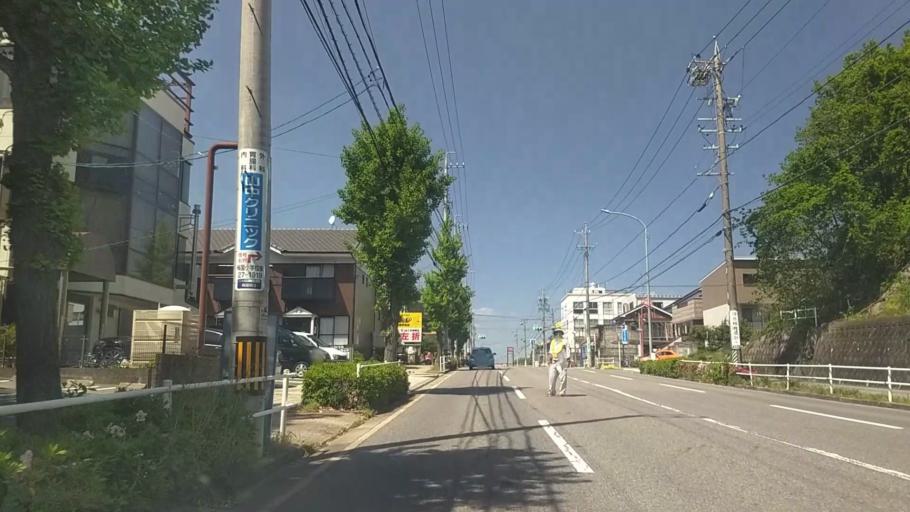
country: JP
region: Aichi
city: Okazaki
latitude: 34.9613
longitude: 137.1717
